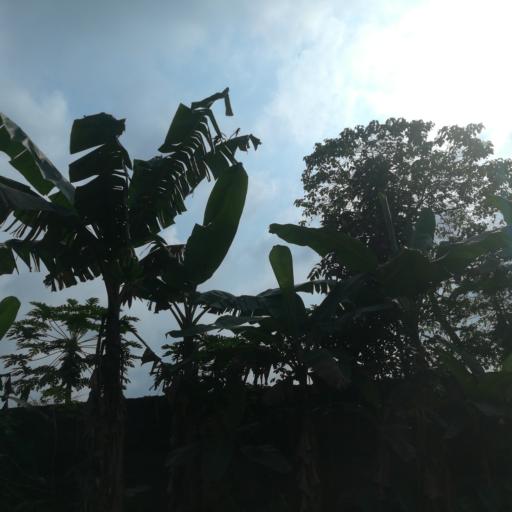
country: NG
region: Rivers
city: Okrika
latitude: 4.7834
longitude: 7.1381
